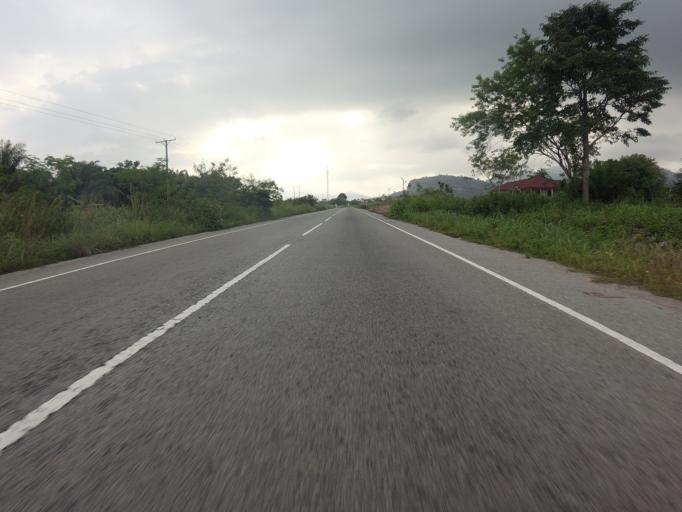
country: GH
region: Volta
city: Ho
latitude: 6.7814
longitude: 0.4652
